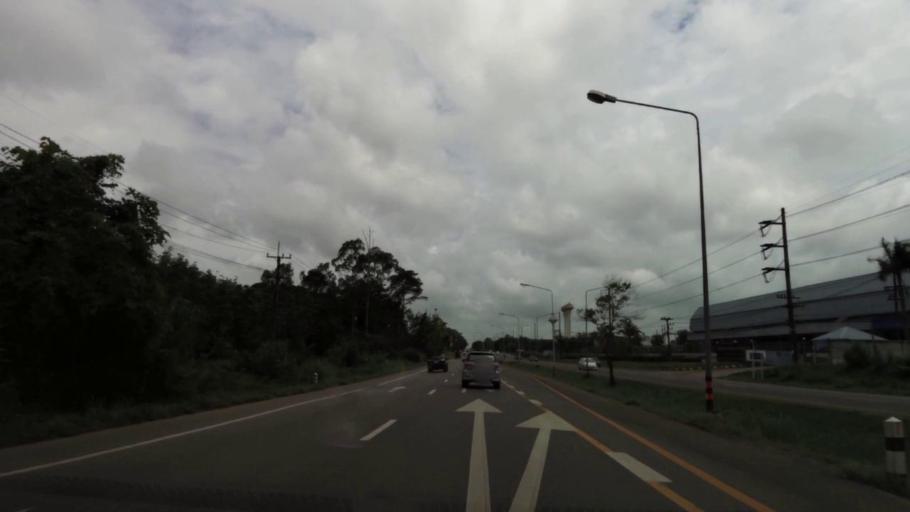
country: TH
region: Chanthaburi
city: Na Yai Am
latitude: 12.7430
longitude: 101.8885
